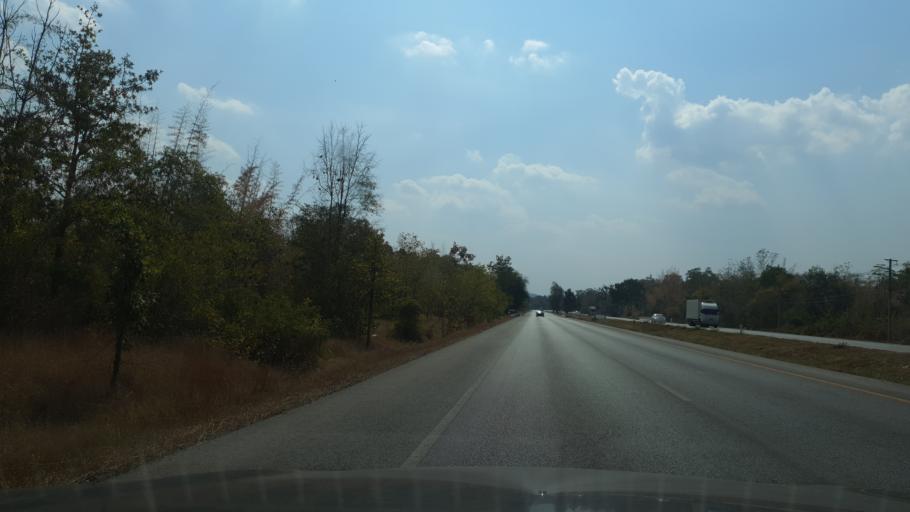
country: TH
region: Lampang
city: Mae Phrik
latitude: 17.4255
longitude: 99.1578
